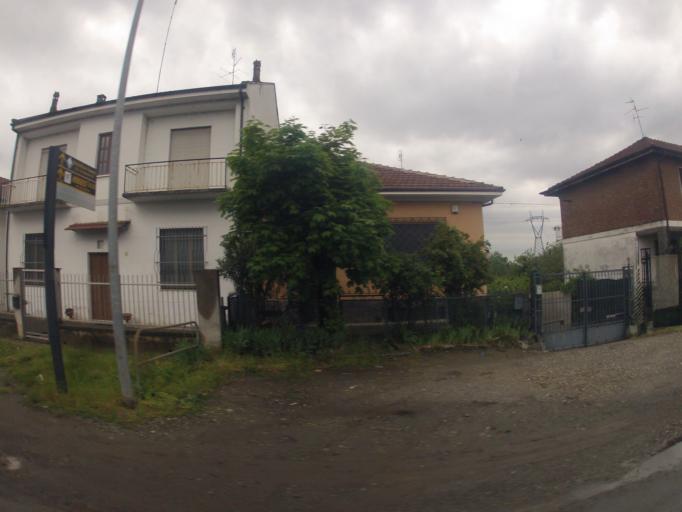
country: IT
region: Piedmont
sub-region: Provincia di Torino
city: Tagliaferro
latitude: 44.9908
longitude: 7.6714
